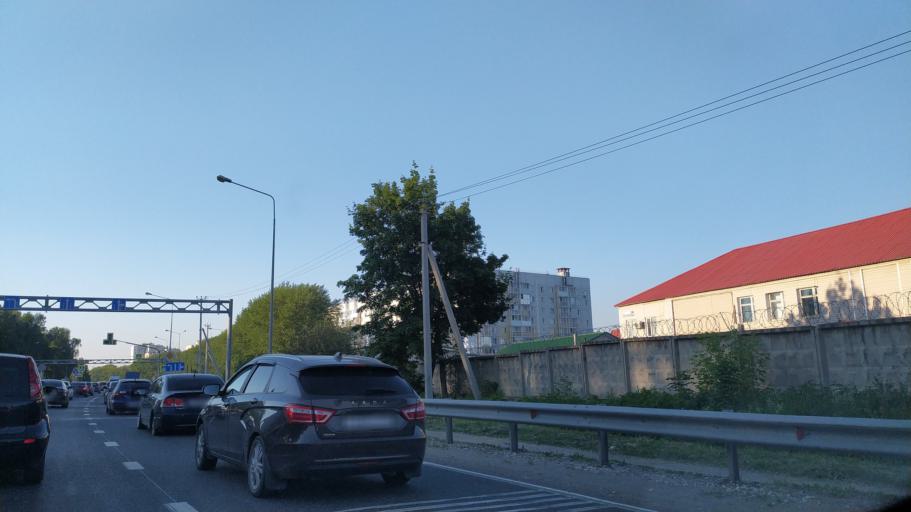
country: RU
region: Chuvashia
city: Kugesi
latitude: 56.0645
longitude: 47.2788
